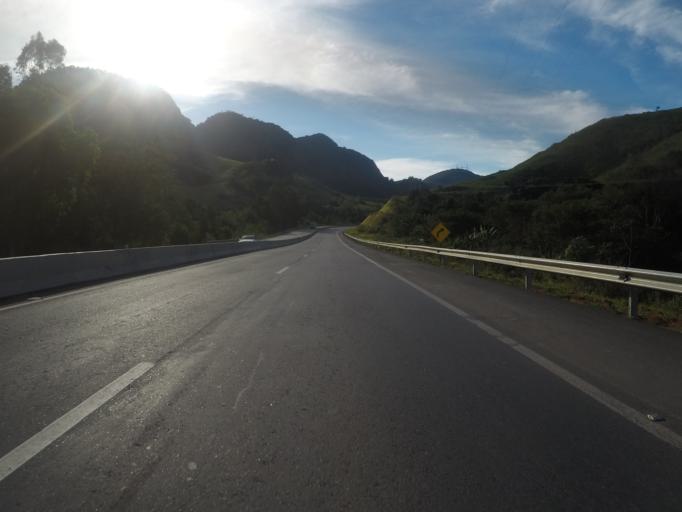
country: BR
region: Espirito Santo
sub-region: Ibiracu
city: Ibiracu
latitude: -19.8460
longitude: -40.3849
